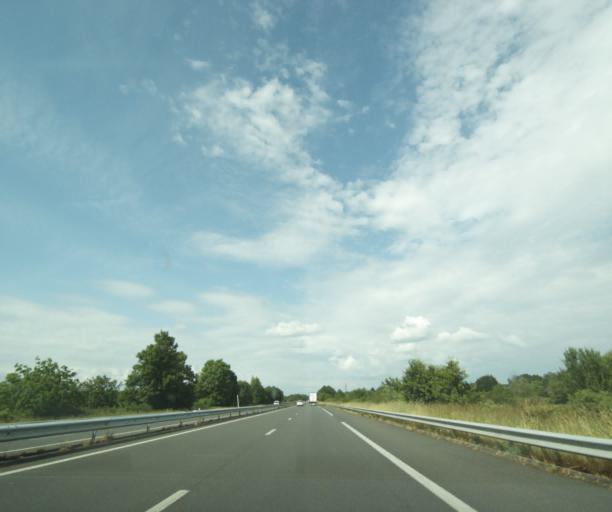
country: FR
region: Pays de la Loire
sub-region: Departement de la Sarthe
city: Vion
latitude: 47.7586
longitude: -0.2317
